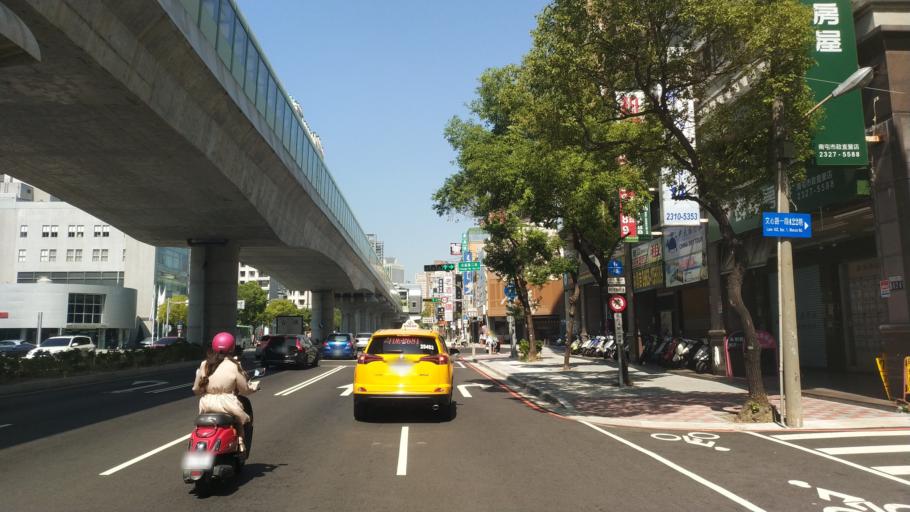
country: TW
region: Taiwan
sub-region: Taichung City
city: Taichung
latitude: 24.1503
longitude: 120.6469
